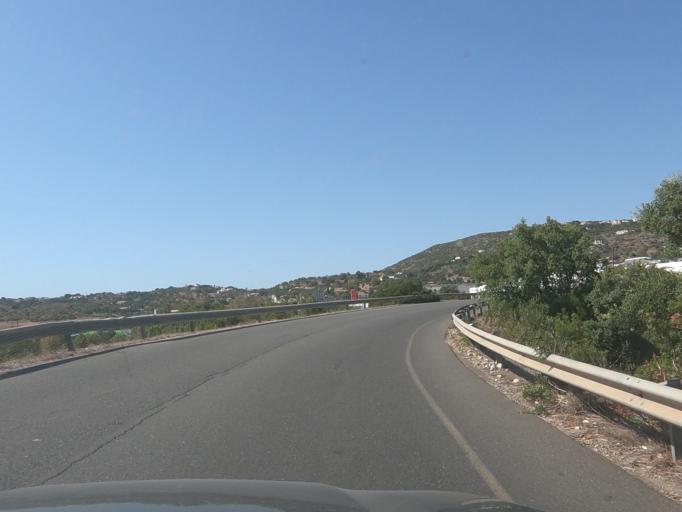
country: PT
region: Faro
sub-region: Faro
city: Santa Barbara de Nexe
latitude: 37.0947
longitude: -7.9976
